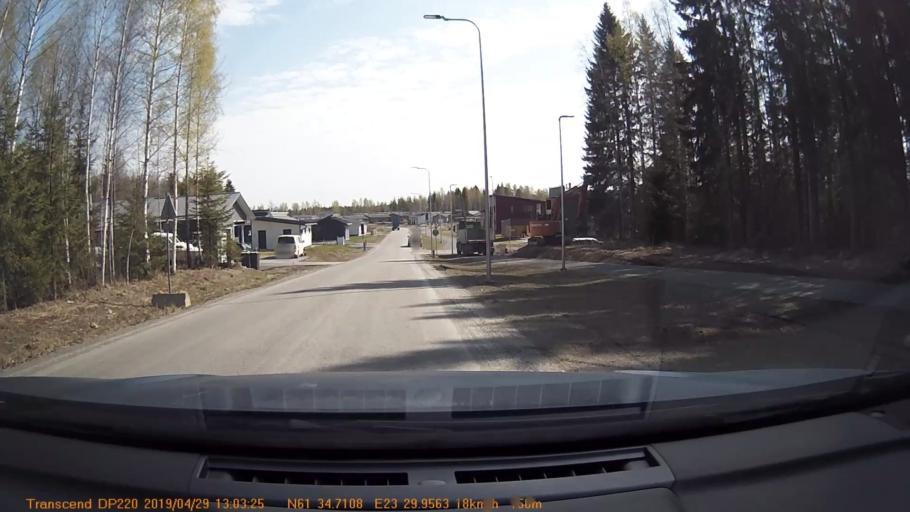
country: FI
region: Pirkanmaa
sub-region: Tampere
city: Yloejaervi
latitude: 61.5786
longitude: 23.4992
